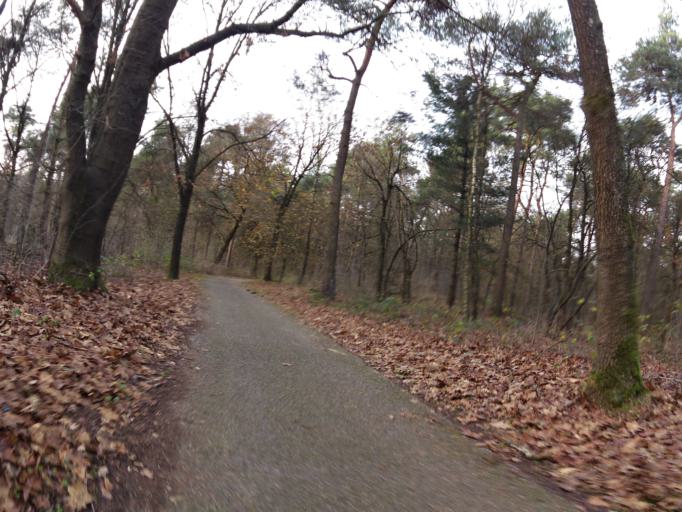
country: NL
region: North Brabant
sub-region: Gemeente Uden
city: Uden
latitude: 51.6853
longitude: 5.6338
